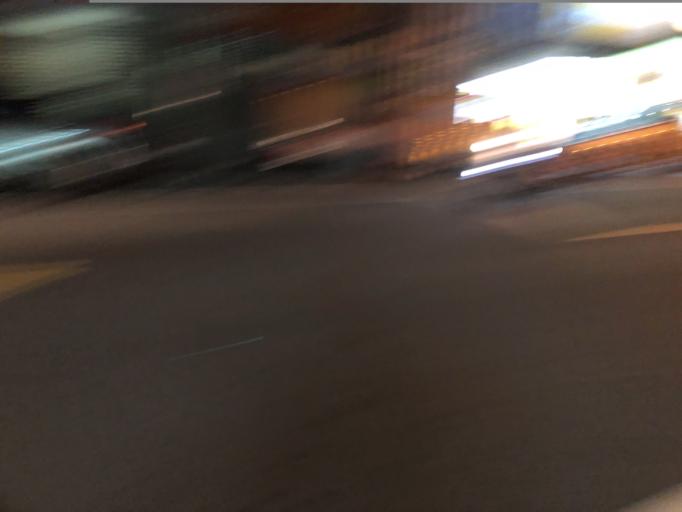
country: TW
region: Taiwan
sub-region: Taoyuan
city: Taoyuan
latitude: 24.9895
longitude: 121.3443
